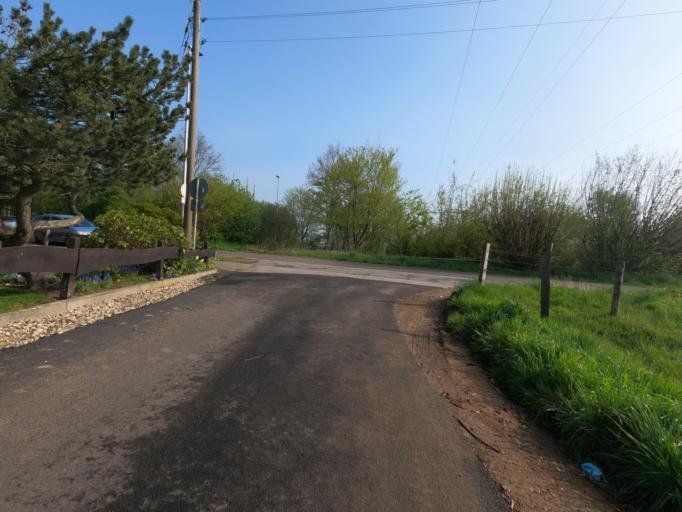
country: DE
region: North Rhine-Westphalia
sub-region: Regierungsbezirk Koln
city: Wassenberg
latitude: 51.0500
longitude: 6.1499
